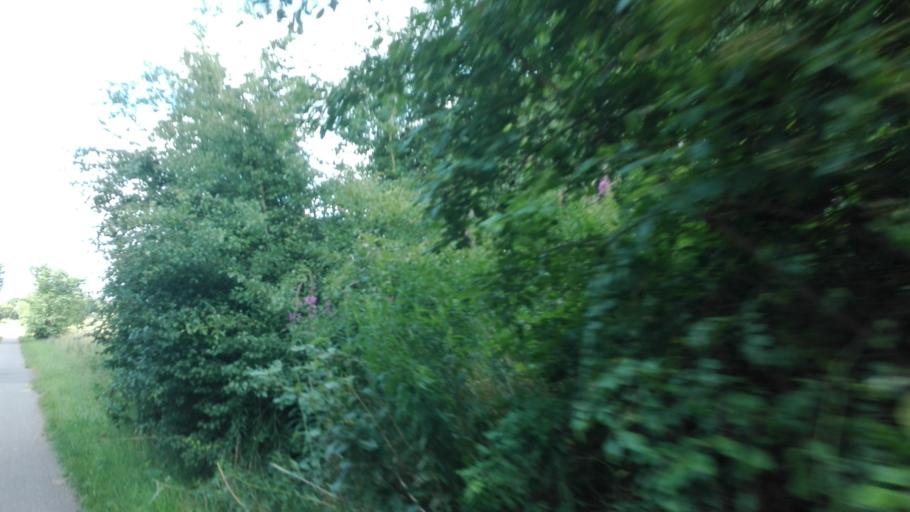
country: DK
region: Central Jutland
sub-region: Silkeborg Kommune
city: Virklund
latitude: 56.0901
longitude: 9.5319
